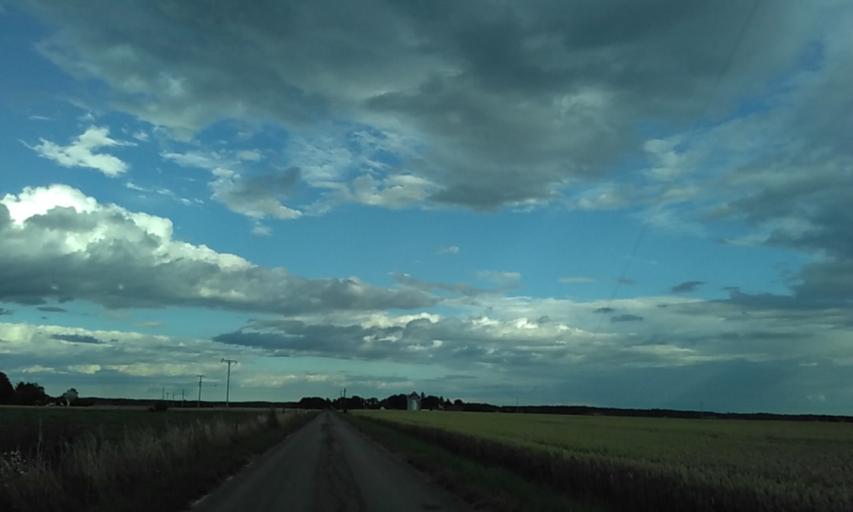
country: SE
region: Vaestra Goetaland
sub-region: Grastorps Kommun
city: Graestorp
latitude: 58.4096
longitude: 12.7230
